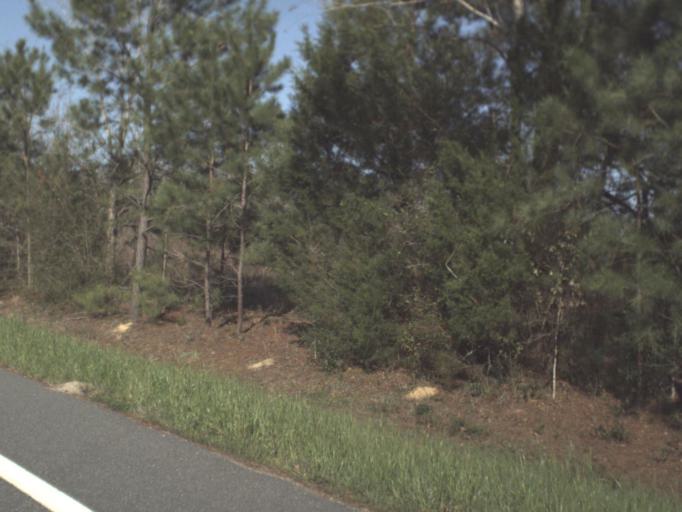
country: US
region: Florida
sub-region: Calhoun County
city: Blountstown
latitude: 30.4339
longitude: -85.1891
